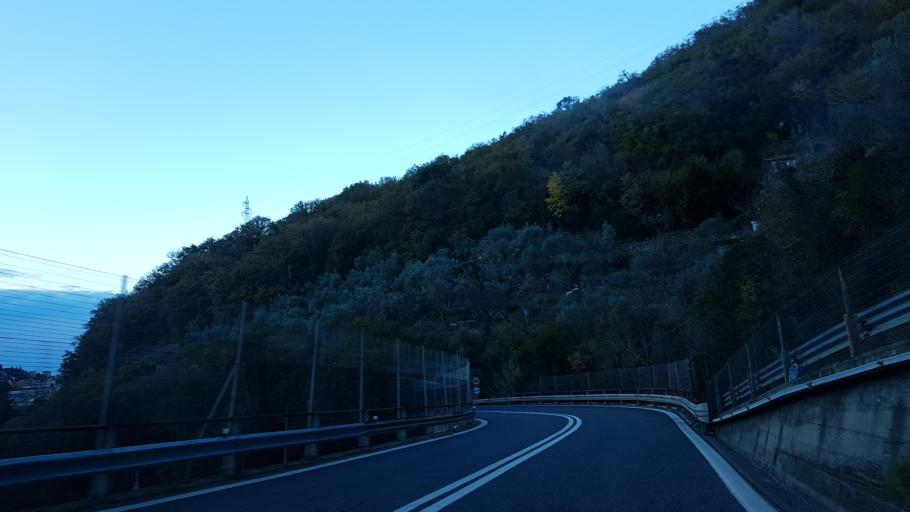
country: IT
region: Liguria
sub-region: Provincia di Genova
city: Avegno
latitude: 44.3745
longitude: 9.1495
